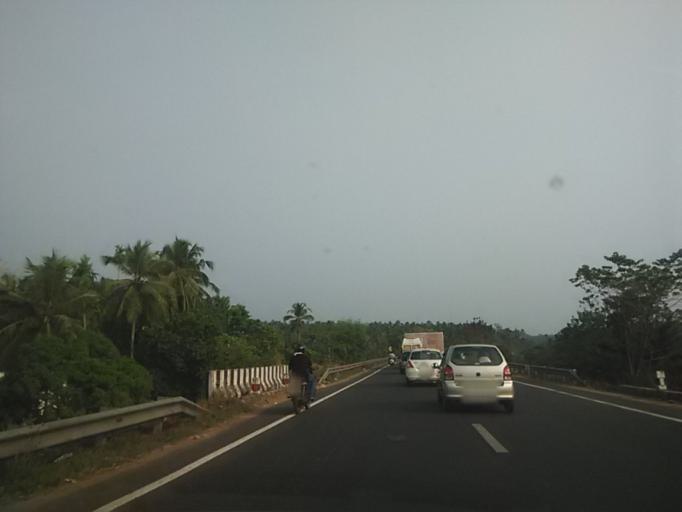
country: IN
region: Kerala
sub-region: Kozhikode
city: Kozhikode
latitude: 11.2989
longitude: 75.7943
